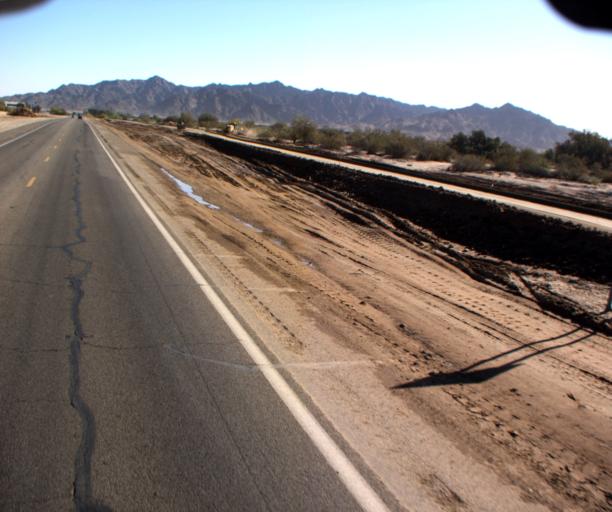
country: US
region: Arizona
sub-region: Yuma County
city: Fortuna Foothills
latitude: 32.7031
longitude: -114.4380
